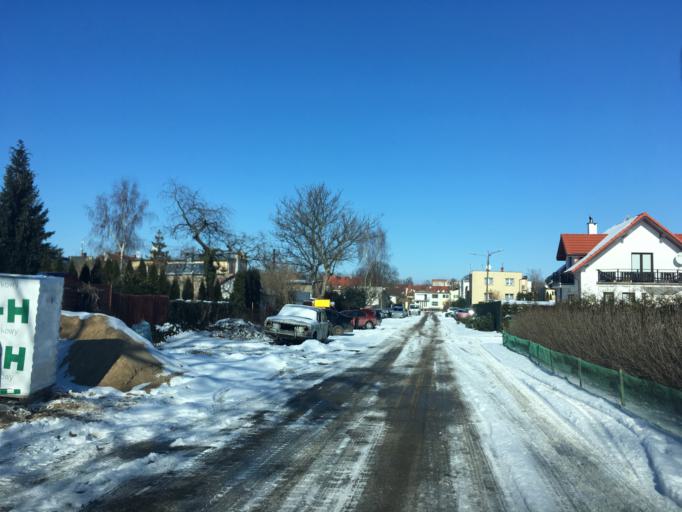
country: PL
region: Pomeranian Voivodeship
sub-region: Slupsk
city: Slupsk
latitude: 54.4572
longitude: 17.0452
